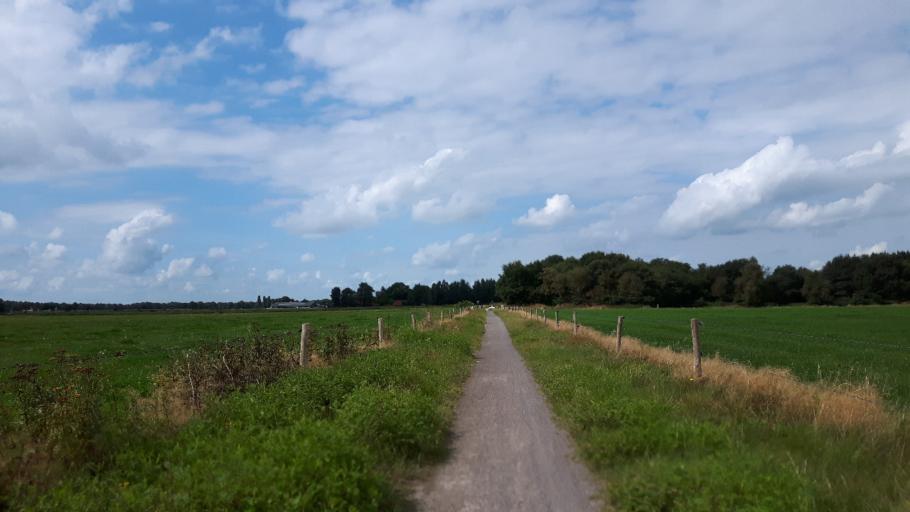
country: NL
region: Groningen
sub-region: Gemeente Leek
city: Leek
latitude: 53.0816
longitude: 6.3291
